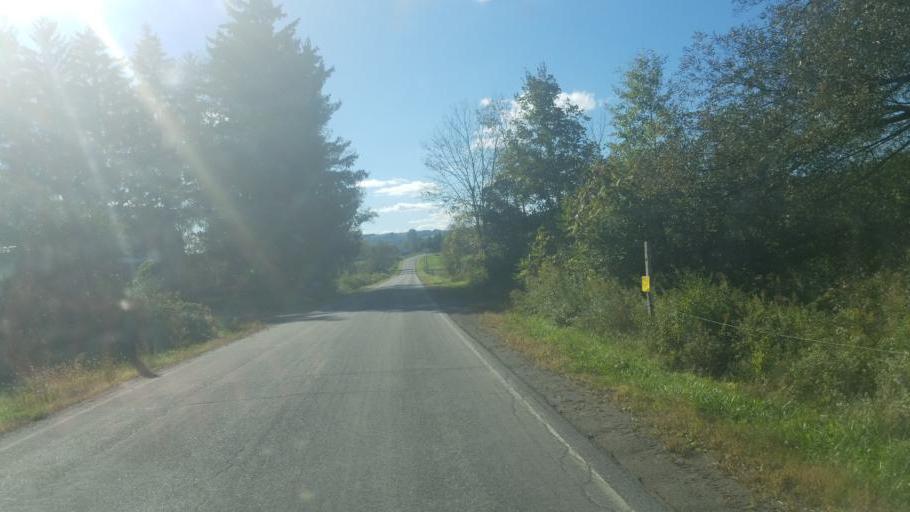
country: US
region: New York
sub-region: Allegany County
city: Friendship
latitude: 42.2746
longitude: -78.2008
